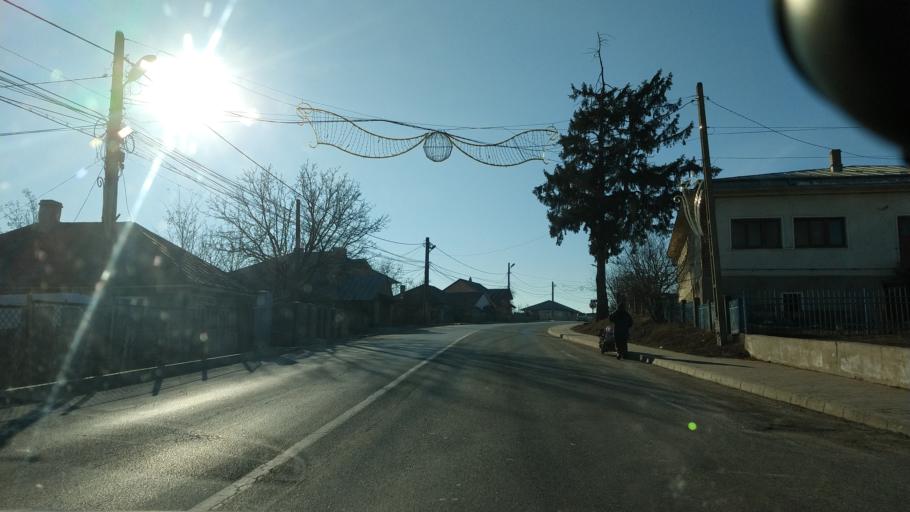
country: RO
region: Iasi
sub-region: Comuna Targu Frumos
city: Targu Frumos
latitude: 47.2041
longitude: 27.0072
